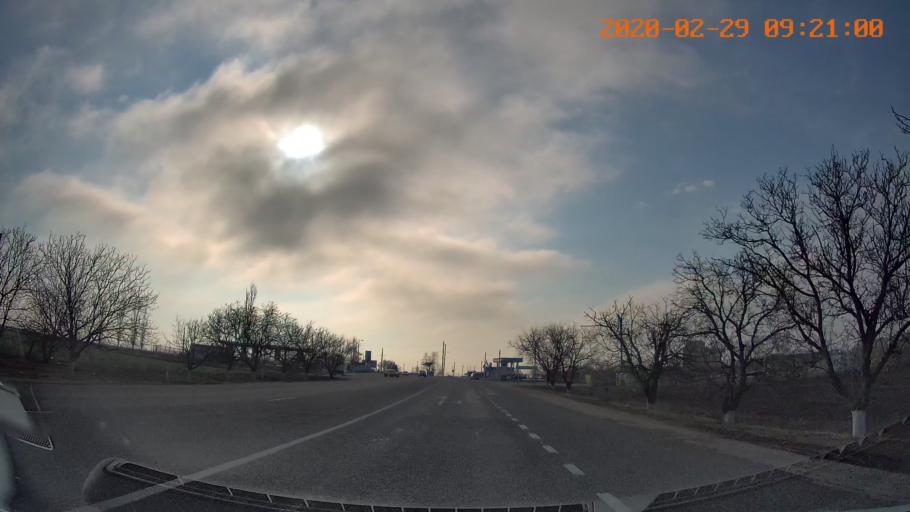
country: MD
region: Telenesti
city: Pervomaisc
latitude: 46.7414
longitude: 29.9542
